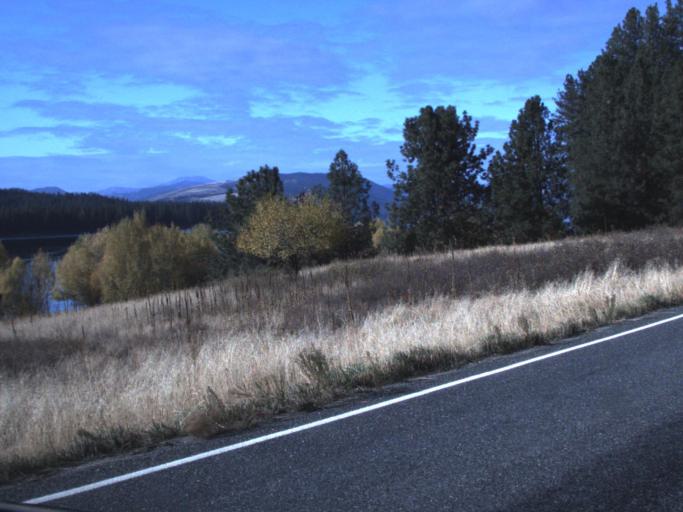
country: US
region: Washington
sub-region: Stevens County
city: Kettle Falls
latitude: 48.2604
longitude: -118.1315
